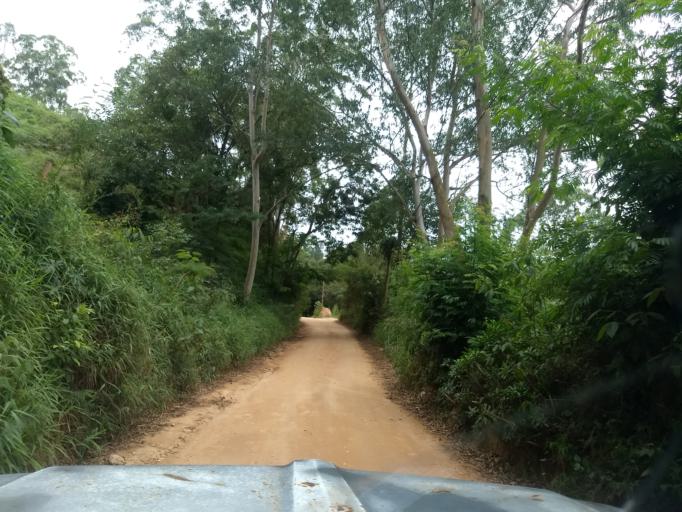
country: BR
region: Sao Paulo
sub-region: Cabreuva
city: Cabreuva
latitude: -23.4082
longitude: -47.1978
